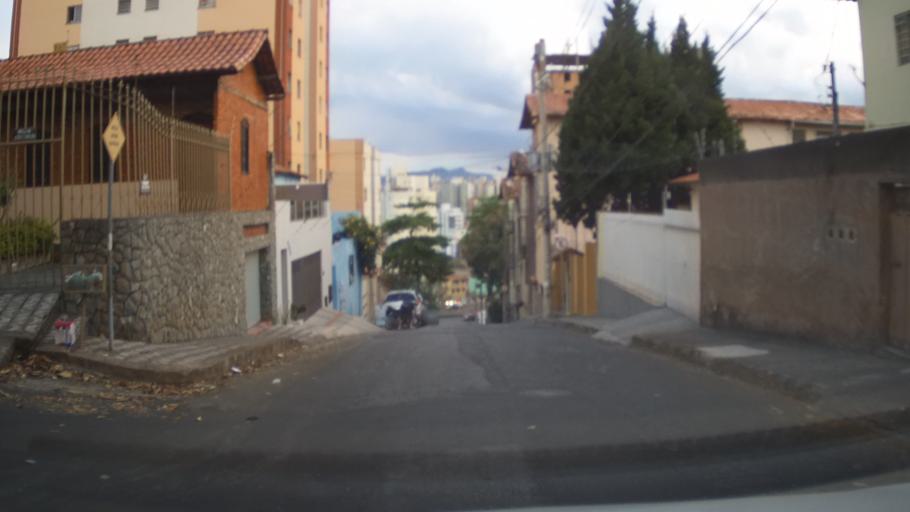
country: BR
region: Minas Gerais
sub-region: Belo Horizonte
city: Belo Horizonte
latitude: -19.9014
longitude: -43.9293
